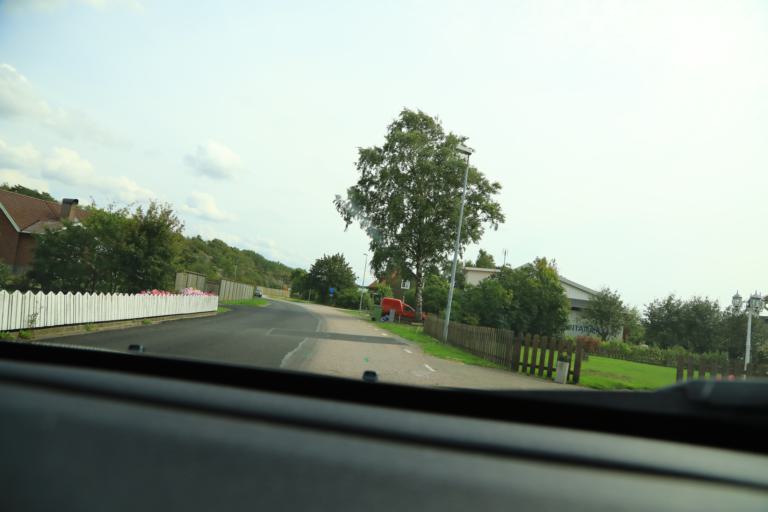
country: SE
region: Halland
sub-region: Varbergs Kommun
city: Varberg
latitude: 57.1727
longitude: 12.2262
